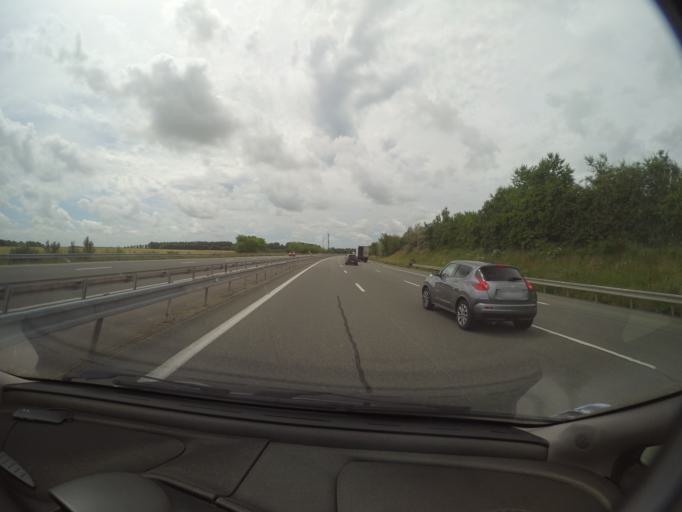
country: FR
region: Centre
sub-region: Departement d'Eure-et-Loir
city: Morancez
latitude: 48.3857
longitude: 1.4913
